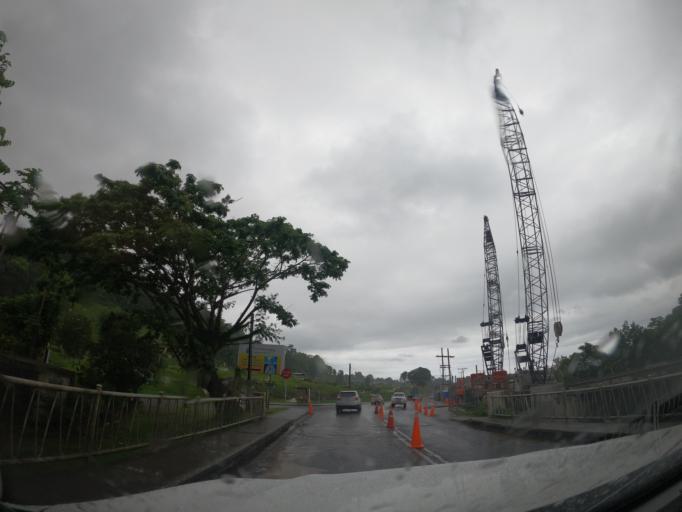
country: FJ
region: Central
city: Suva
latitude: -18.1153
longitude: 178.4312
